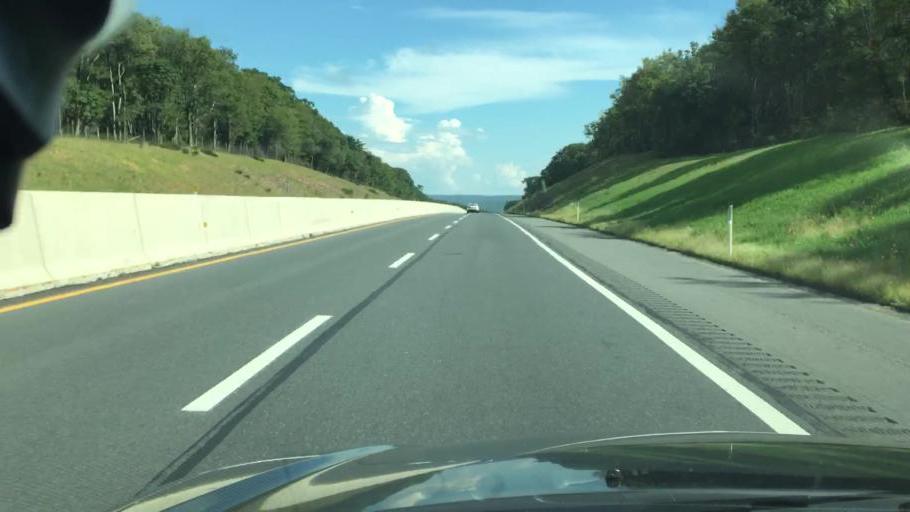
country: US
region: Pennsylvania
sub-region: Carbon County
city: Towamensing Trails
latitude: 41.0330
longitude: -75.6564
